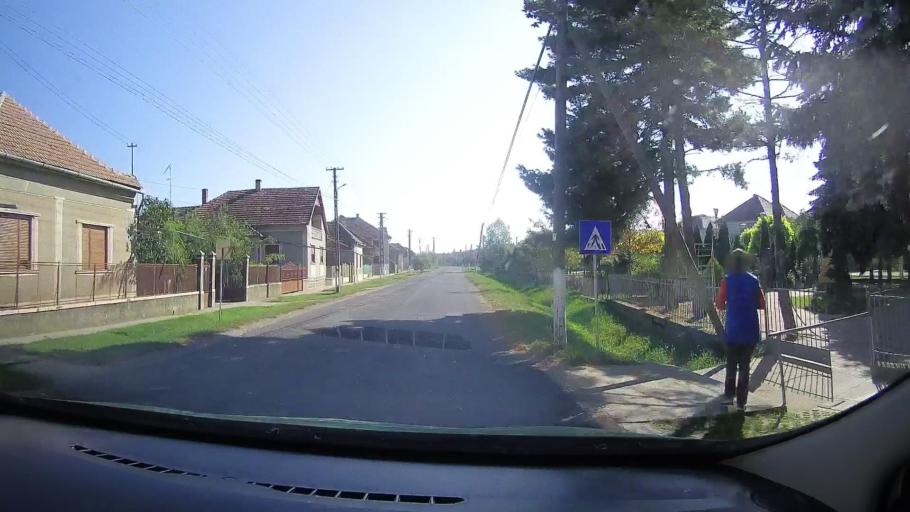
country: RO
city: Foieni
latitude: 47.6972
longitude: 22.3850
